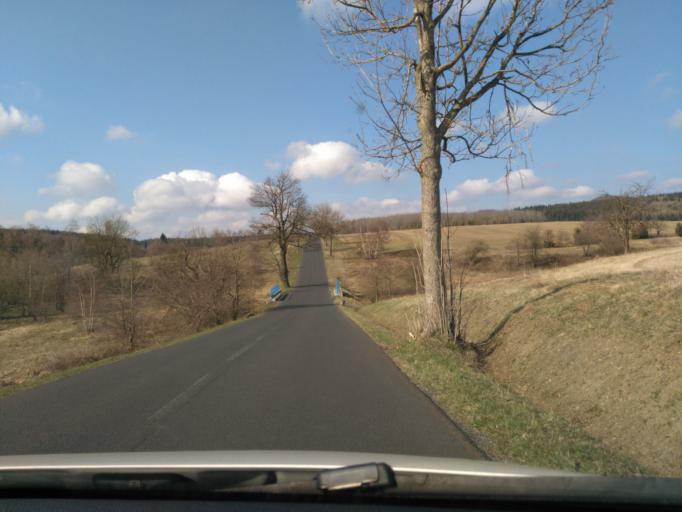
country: DE
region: Saxony
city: Johstadt
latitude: 50.4610
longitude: 13.1210
